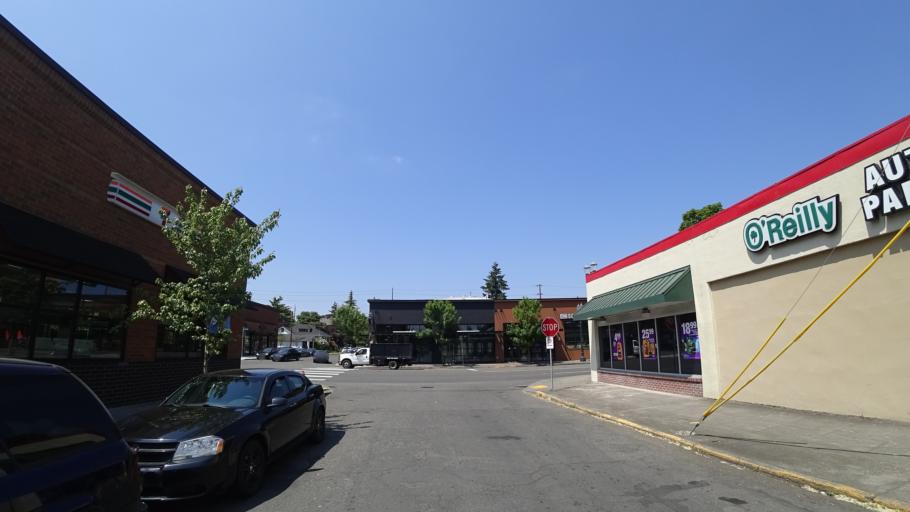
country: US
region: Oregon
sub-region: Multnomah County
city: Portland
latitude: 45.5606
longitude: -122.6612
